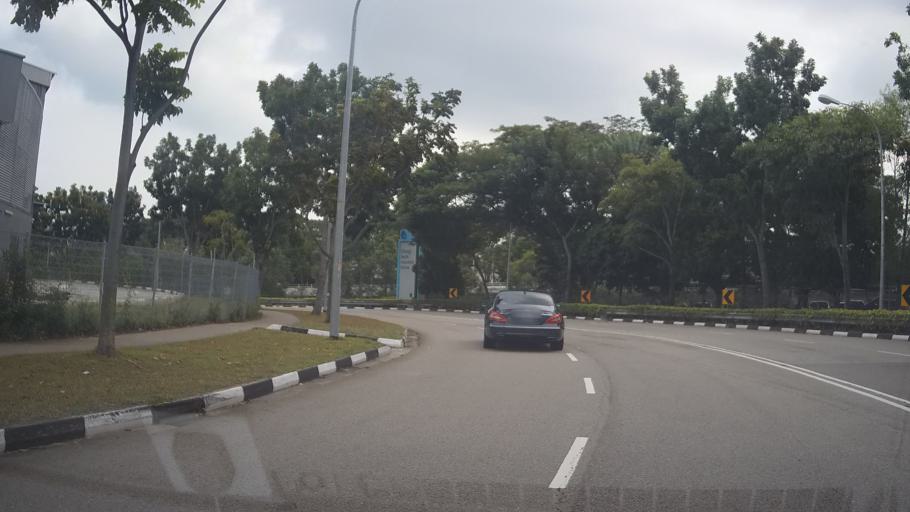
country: SG
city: Singapore
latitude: 1.3494
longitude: 103.9668
